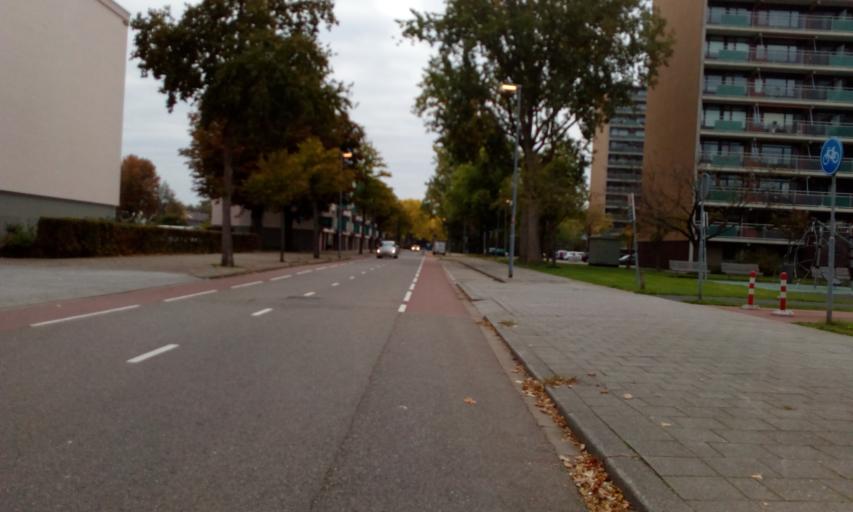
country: NL
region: South Holland
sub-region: Gemeente Spijkenisse
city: Spijkenisse
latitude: 51.8500
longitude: 4.3692
